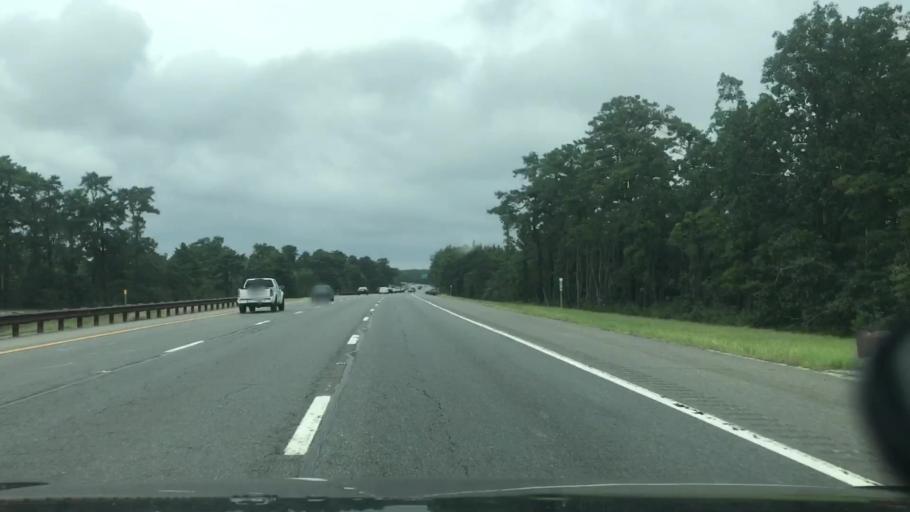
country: US
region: New Jersey
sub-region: Ocean County
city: Forked River
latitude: 39.8252
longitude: -74.2269
